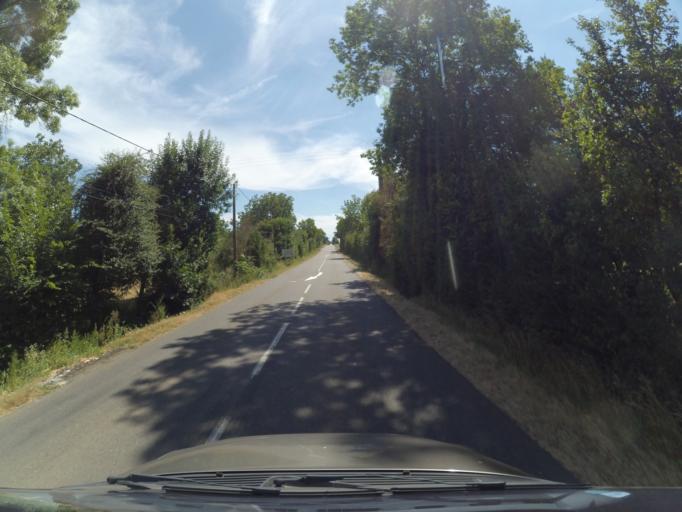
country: FR
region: Poitou-Charentes
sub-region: Departement de la Vienne
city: Usson-du-Poitou
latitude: 46.2686
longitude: 0.5201
